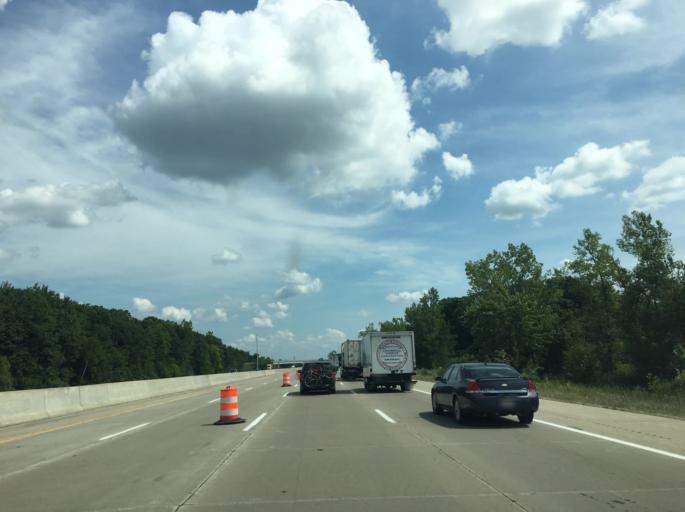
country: US
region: Michigan
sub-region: Saginaw County
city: Birch Run
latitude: 43.2728
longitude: -83.7986
